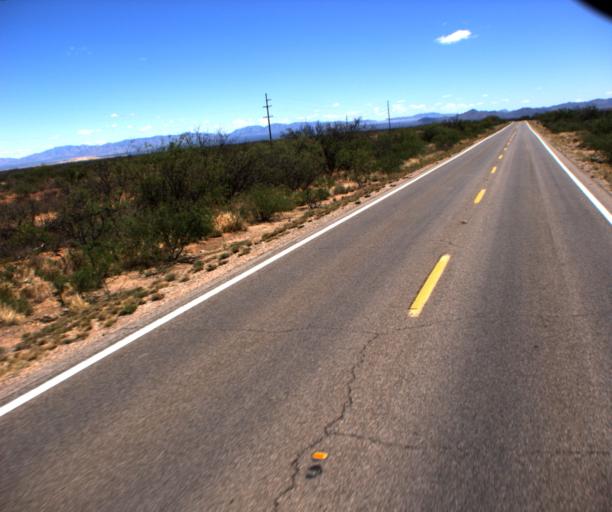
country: US
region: Arizona
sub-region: Cochise County
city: Huachuca City
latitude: 31.6934
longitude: -110.3213
